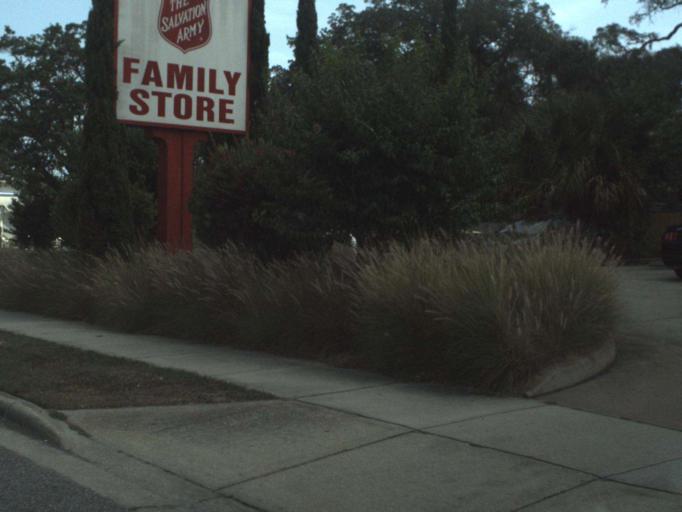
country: US
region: Florida
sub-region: Volusia County
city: Holly Hill
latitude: 29.2518
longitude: -81.0448
